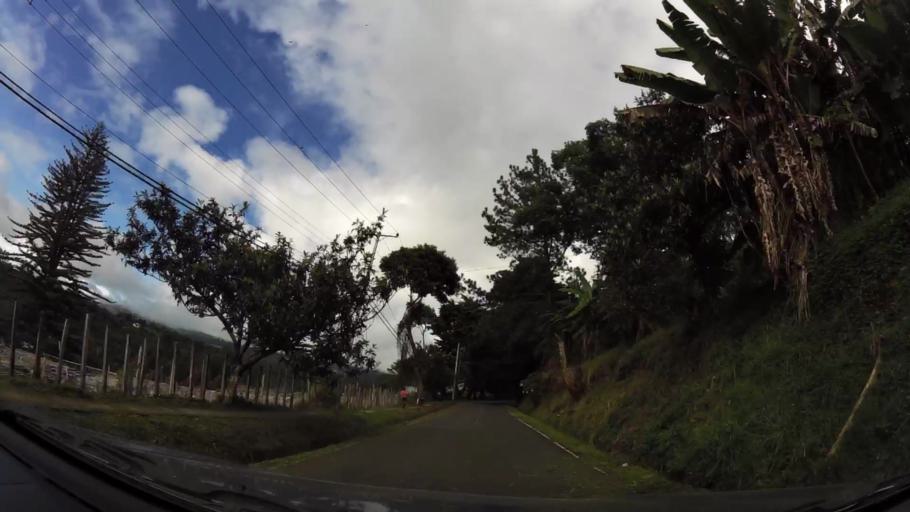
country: PA
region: Chiriqui
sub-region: Distrito Boquete
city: Boquete
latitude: 8.7958
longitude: -82.4390
